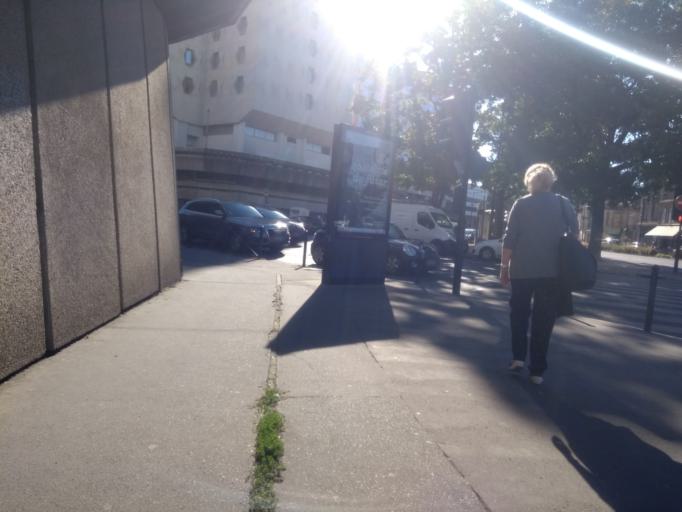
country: FR
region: Aquitaine
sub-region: Departement de la Gironde
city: Bordeaux
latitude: 44.8398
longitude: -0.5861
